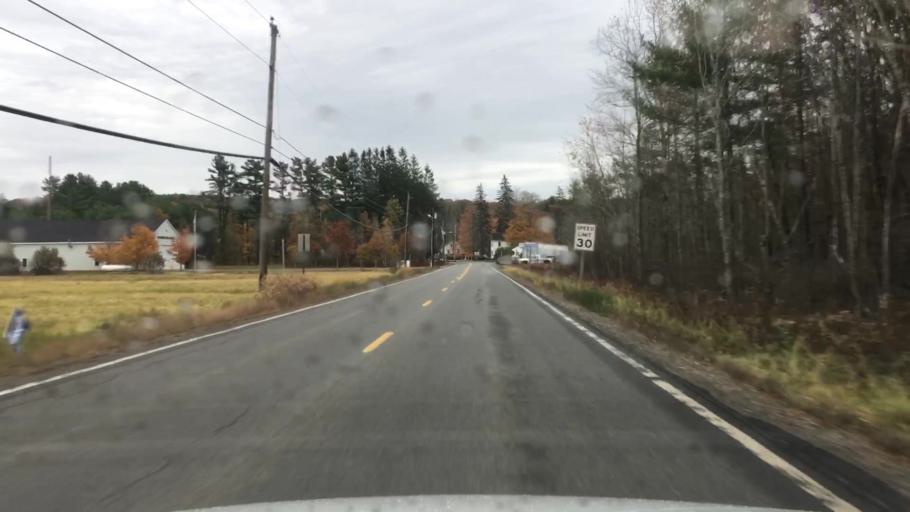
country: US
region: Maine
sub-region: Lincoln County
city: Jefferson
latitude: 44.2019
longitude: -69.4598
